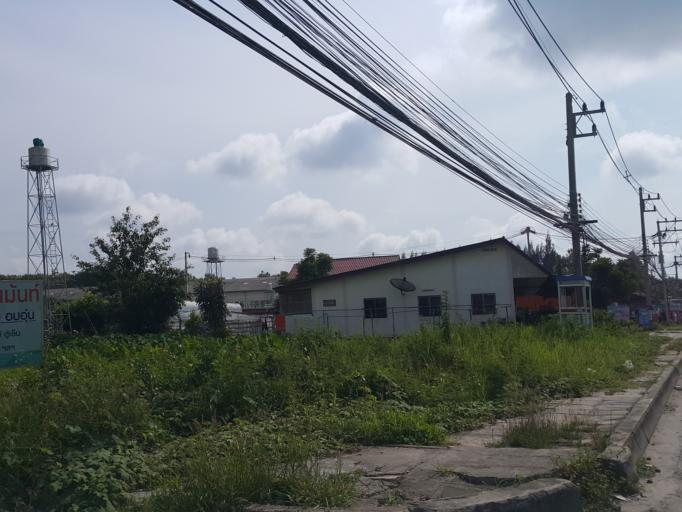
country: TH
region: Chiang Mai
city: San Sai
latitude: 18.8899
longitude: 99.0245
